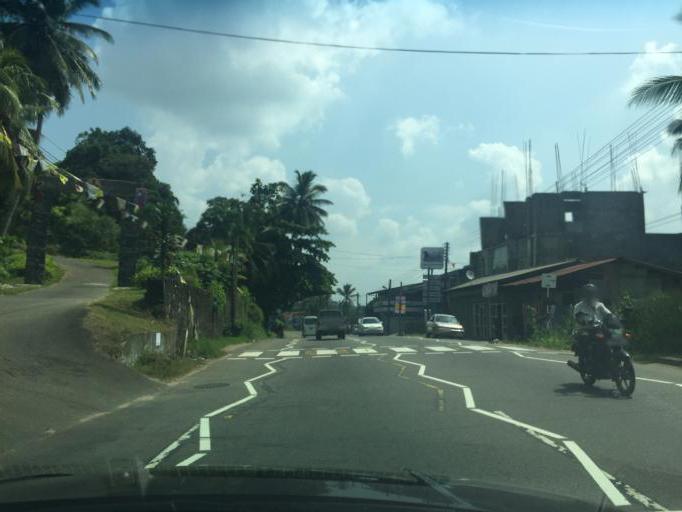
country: LK
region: Western
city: Horana South
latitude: 6.7202
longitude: 80.0486
